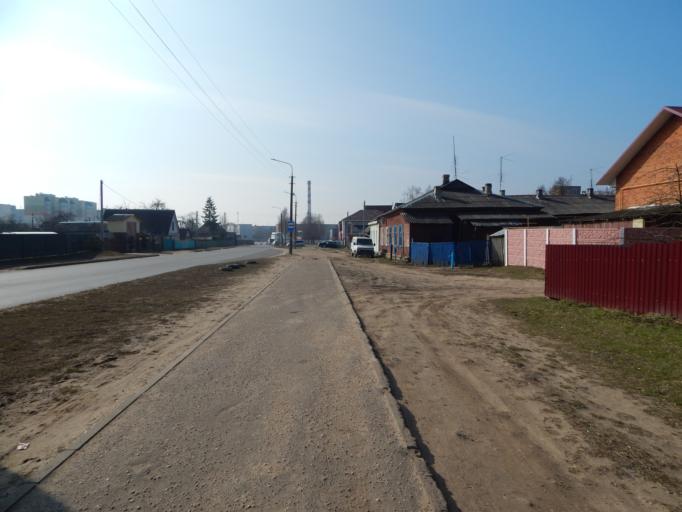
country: BY
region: Minsk
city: Horad Barysaw
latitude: 54.2454
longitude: 28.5093
